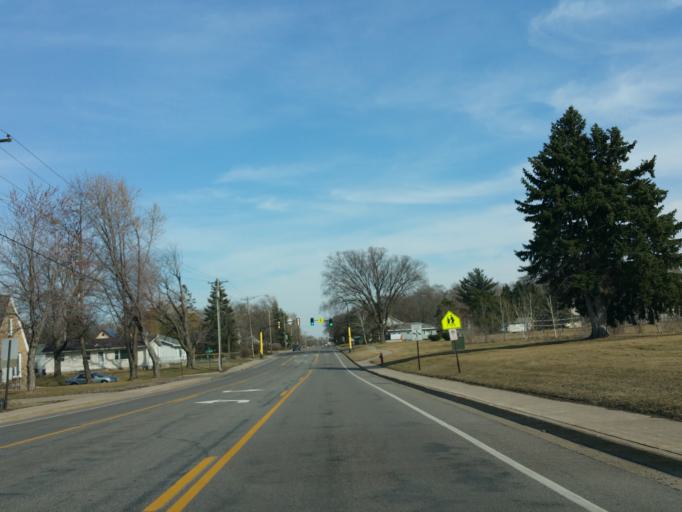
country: US
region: Minnesota
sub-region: Hennepin County
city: Bloomington
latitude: 44.8479
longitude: -93.2554
